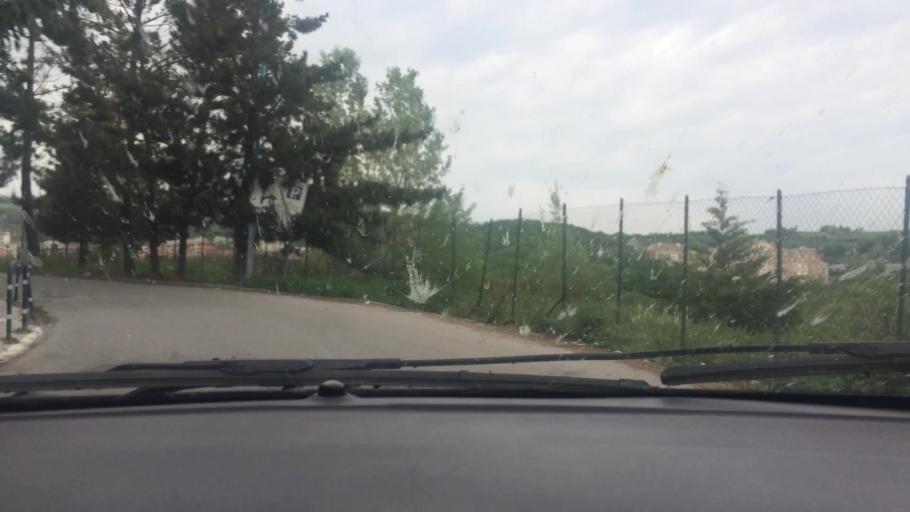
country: IT
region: Basilicate
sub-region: Provincia di Potenza
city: Potenza
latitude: 40.6519
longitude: 15.8083
